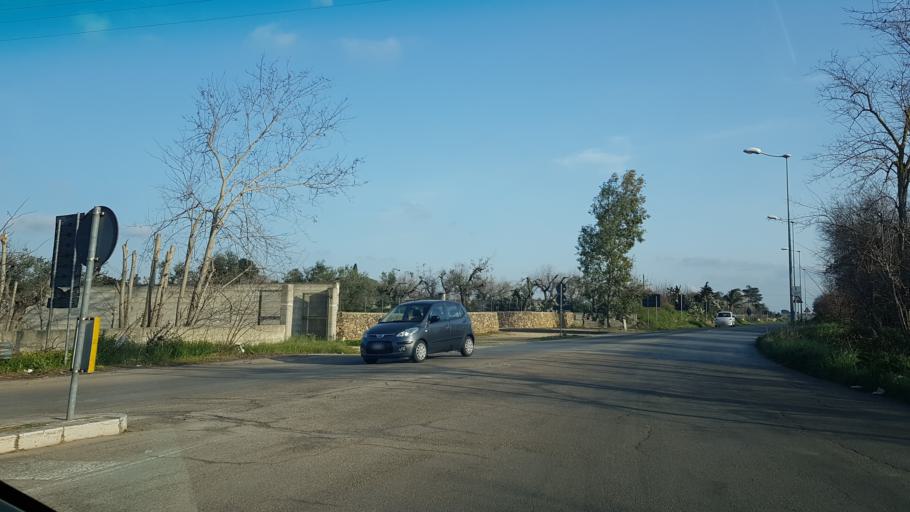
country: IT
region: Apulia
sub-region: Provincia di Lecce
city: Squinzano
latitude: 40.4274
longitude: 18.0532
